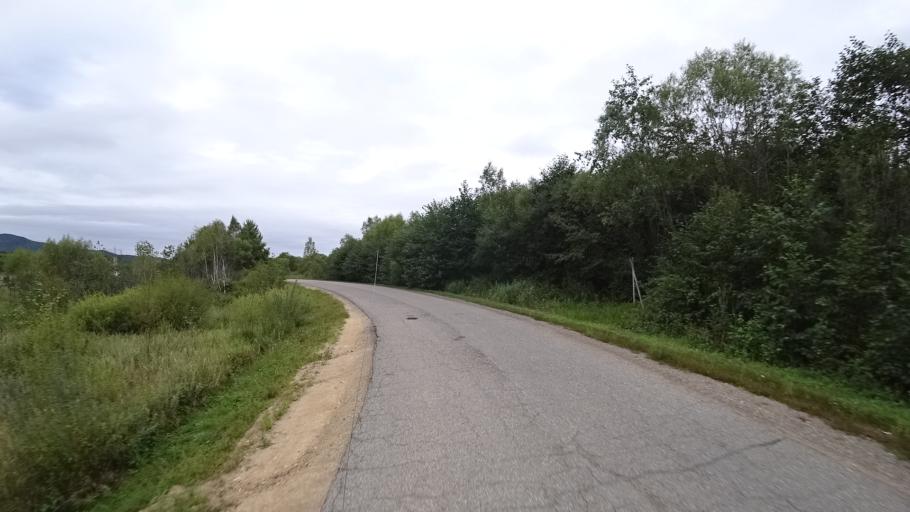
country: RU
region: Primorskiy
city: Rettikhovka
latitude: 44.1667
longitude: 132.7892
